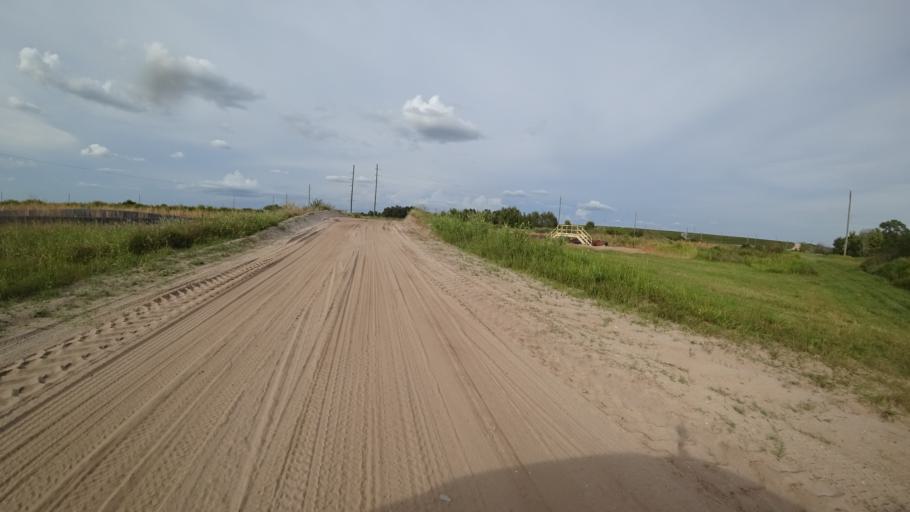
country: US
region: Florida
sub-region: Hardee County
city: Wauchula
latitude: 27.5290
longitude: -82.0723
